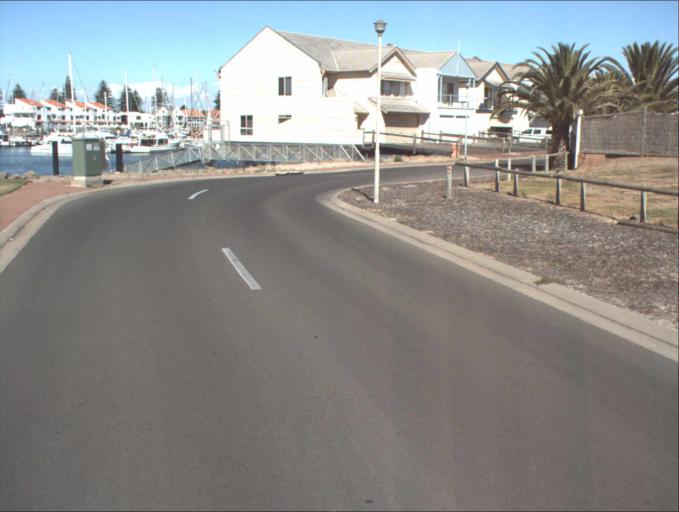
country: AU
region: South Australia
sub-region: Port Adelaide Enfield
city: Birkenhead
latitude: -34.7878
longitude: 138.4847
